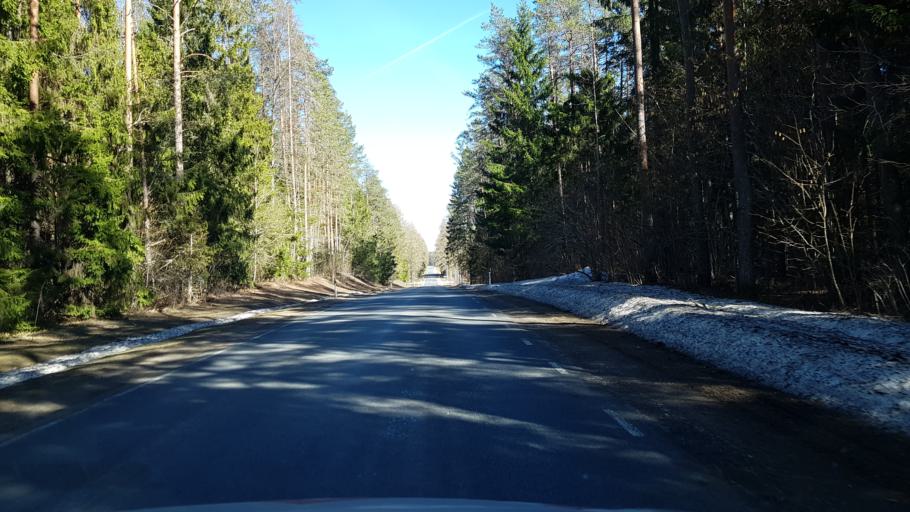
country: EE
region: Laeaene-Virumaa
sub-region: Vinni vald
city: Vinni
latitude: 59.2737
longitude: 26.6251
